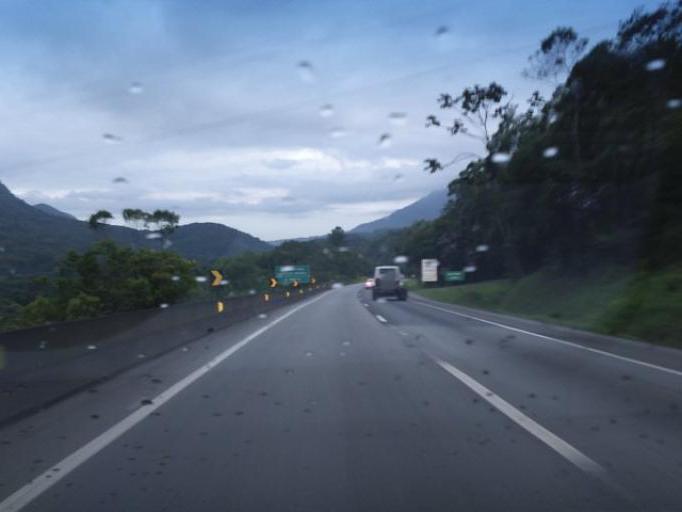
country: BR
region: Parana
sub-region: Guaratuba
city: Guaratuba
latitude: -25.9286
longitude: -48.9127
